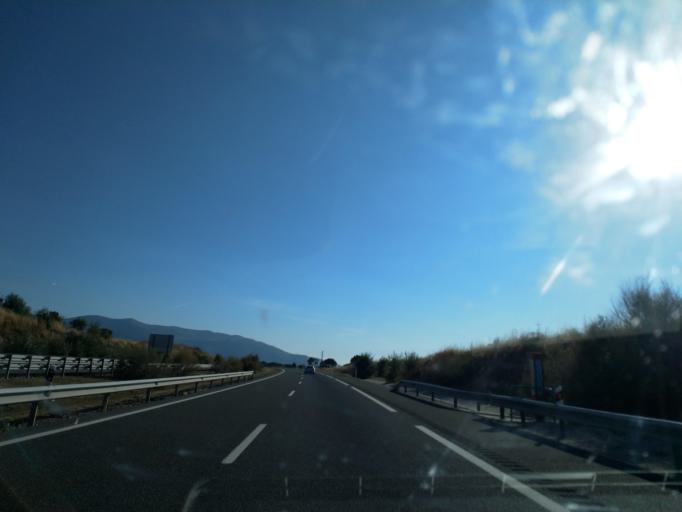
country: ES
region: Castille and Leon
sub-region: Provincia de Segovia
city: Segovia
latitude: 40.8930
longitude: -4.1132
